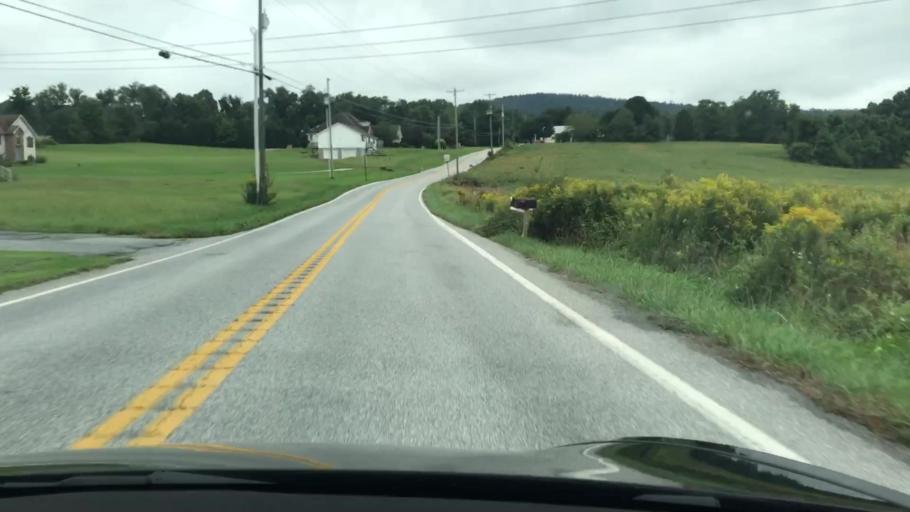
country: US
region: Pennsylvania
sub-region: York County
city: Dillsburg
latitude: 40.1255
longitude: -76.9596
